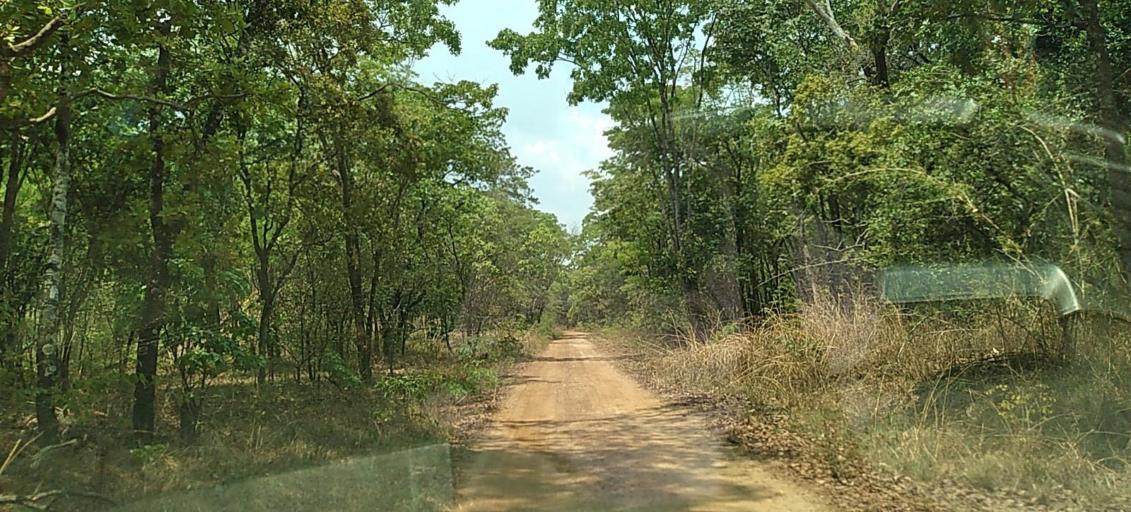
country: ZM
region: Copperbelt
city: Chingola
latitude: -12.7861
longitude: 27.6630
